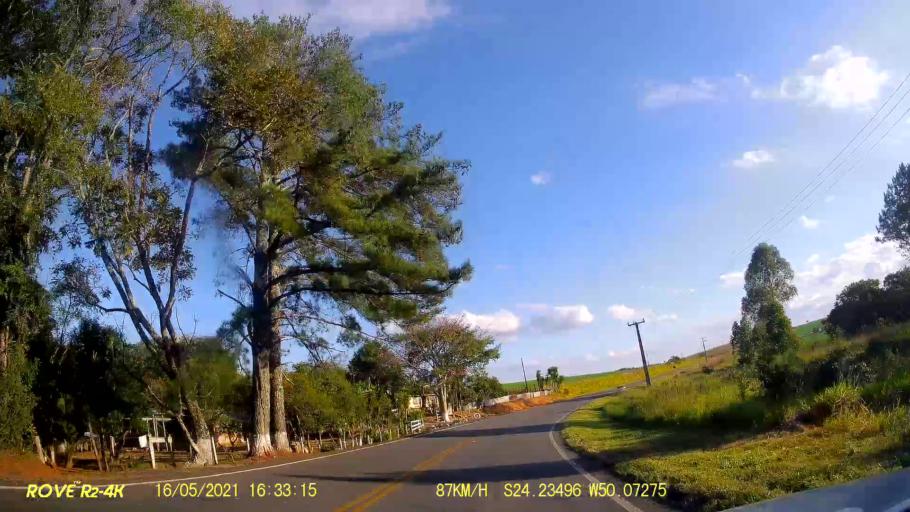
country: BR
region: Parana
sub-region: Pirai Do Sul
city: Pirai do Sul
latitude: -24.2347
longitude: -50.0730
